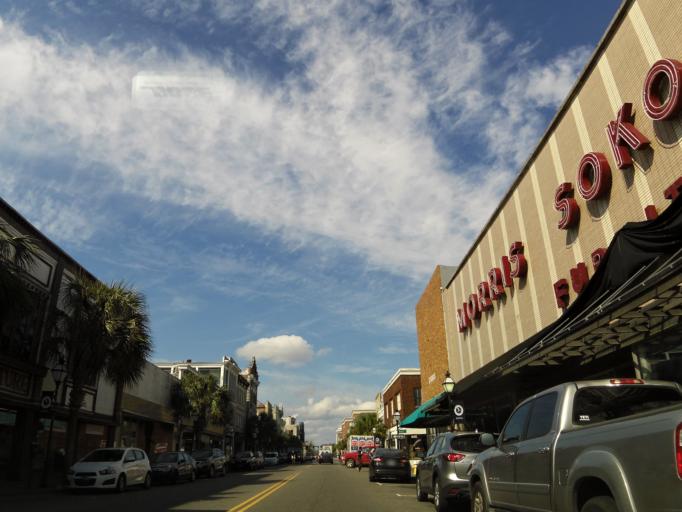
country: US
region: South Carolina
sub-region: Charleston County
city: Charleston
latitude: 32.7908
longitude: -79.9397
